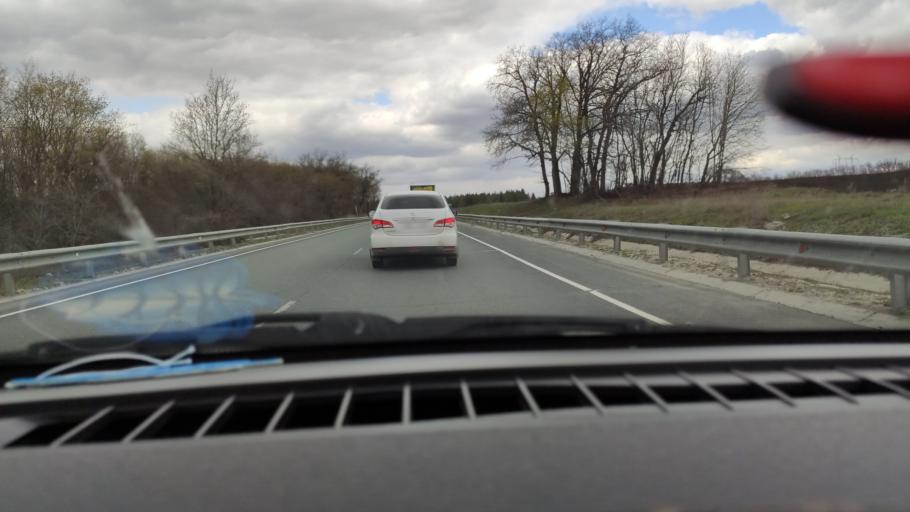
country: RU
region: Saratov
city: Vol'sk
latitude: 52.1039
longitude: 47.4456
